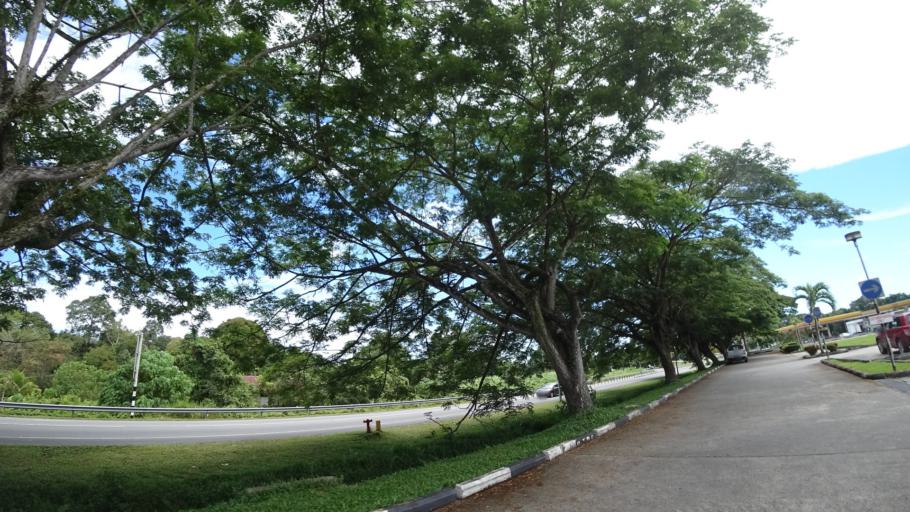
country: BN
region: Tutong
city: Tutong
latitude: 4.7683
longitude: 114.8220
